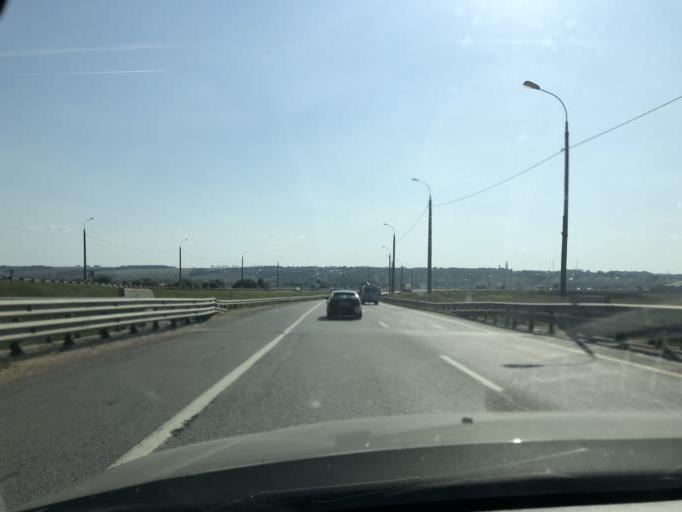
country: RU
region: Moskovskaya
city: Danki
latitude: 54.8676
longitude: 37.5024
